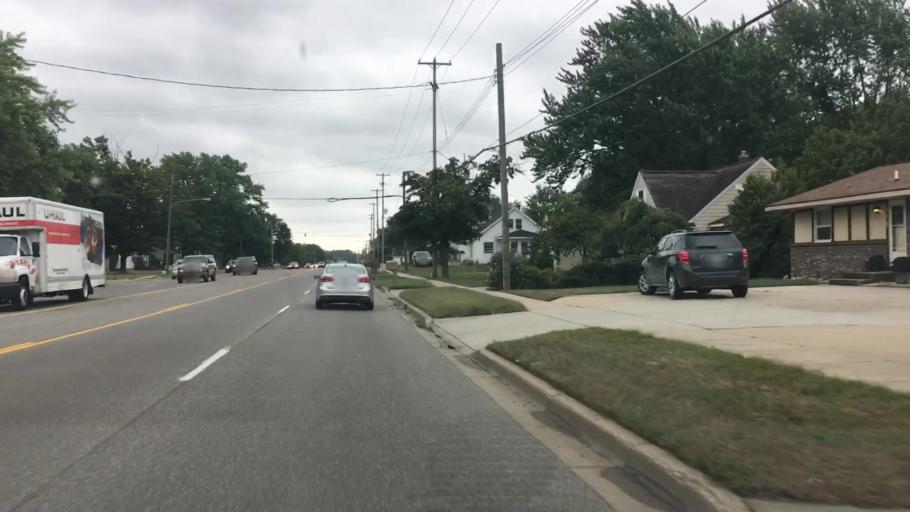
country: US
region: Michigan
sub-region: Ottawa County
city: Jenison
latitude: 42.9071
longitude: -85.8058
